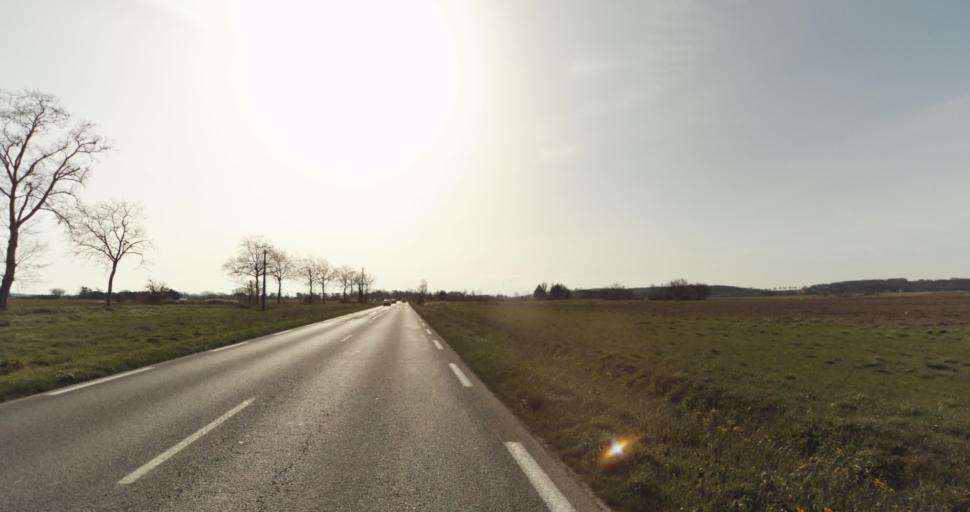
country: FR
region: Midi-Pyrenees
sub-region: Departement du Tarn
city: Saint-Sulpice-la-Pointe
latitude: 43.7545
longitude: 1.7198
